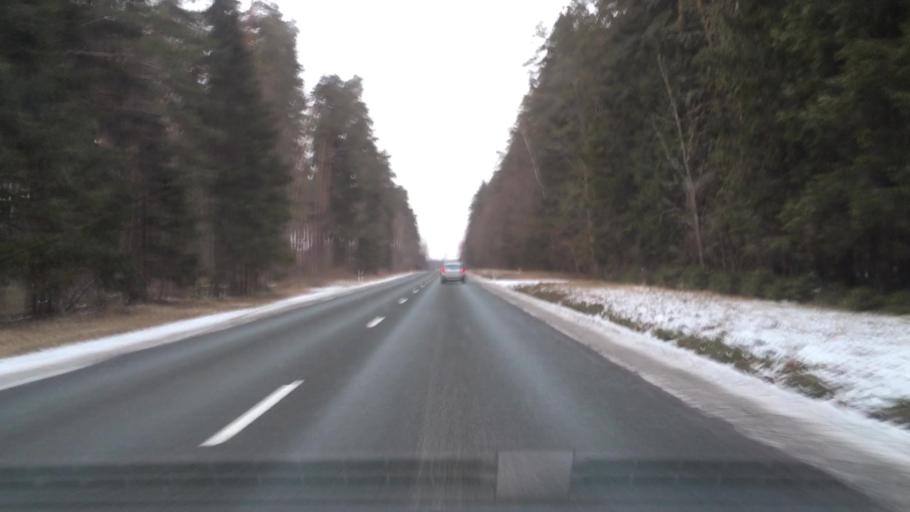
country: LV
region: Valmieras Rajons
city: Valmiera
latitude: 57.5037
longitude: 25.4200
